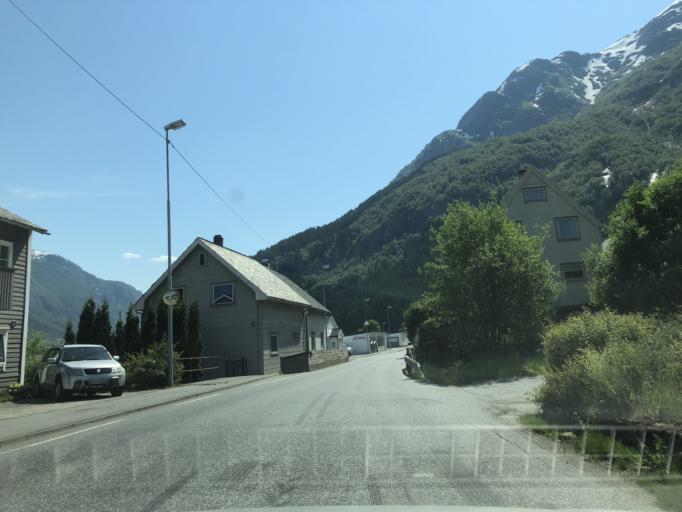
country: NO
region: Hordaland
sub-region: Odda
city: Odda
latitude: 60.0826
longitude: 6.5310
